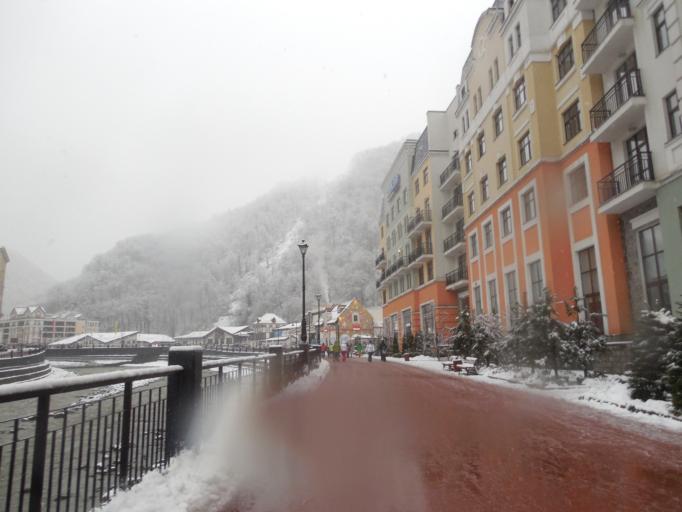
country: RU
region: Krasnodarskiy
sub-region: Sochi City
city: Krasnaya Polyana
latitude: 43.6718
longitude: 40.2941
